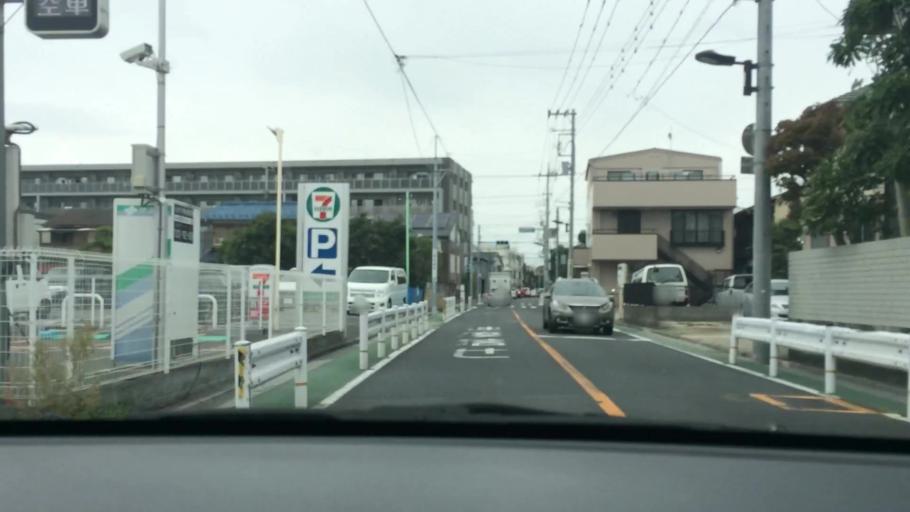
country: JP
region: Chiba
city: Matsudo
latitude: 35.7422
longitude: 139.8918
